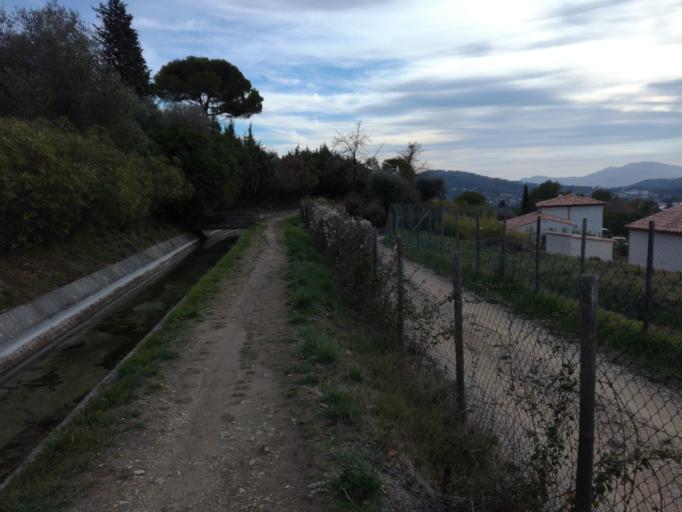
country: FR
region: Provence-Alpes-Cote d'Azur
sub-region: Departement des Alpes-Maritimes
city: Mouans-Sartoux
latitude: 43.6214
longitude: 6.9813
